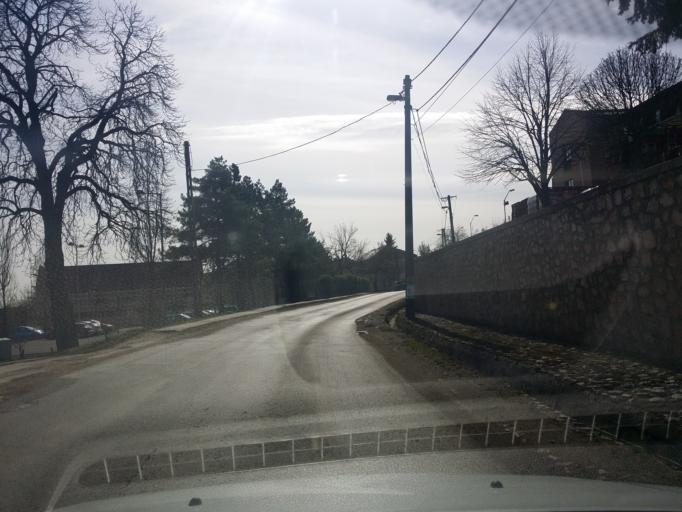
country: HU
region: Baranya
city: Villany
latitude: 45.8752
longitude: 18.4566
